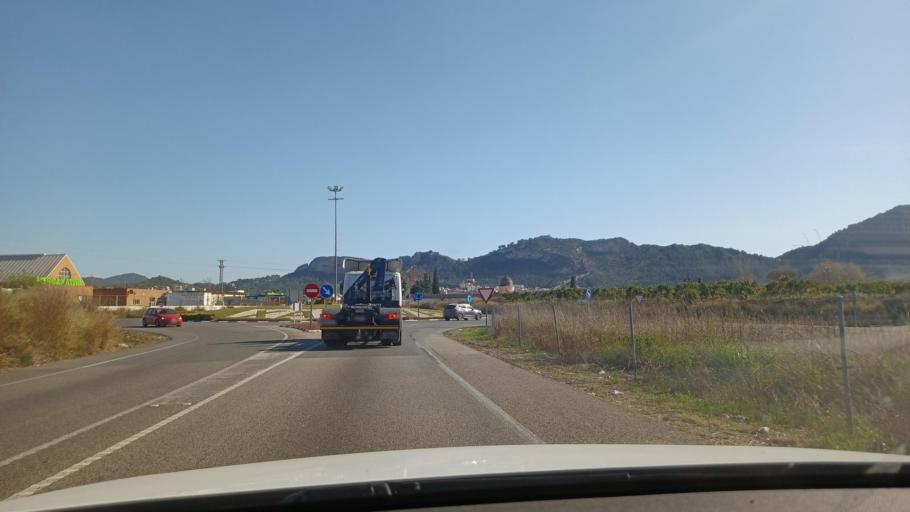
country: ES
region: Valencia
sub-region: Provincia de Valencia
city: Llosa de Ranes
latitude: 39.0025
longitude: -0.5294
